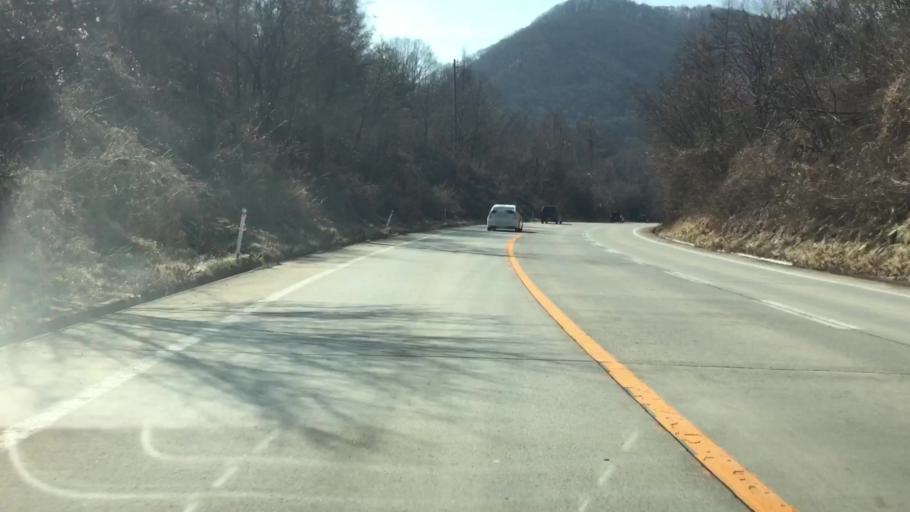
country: JP
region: Nagano
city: Saku
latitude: 36.3015
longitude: 138.6466
